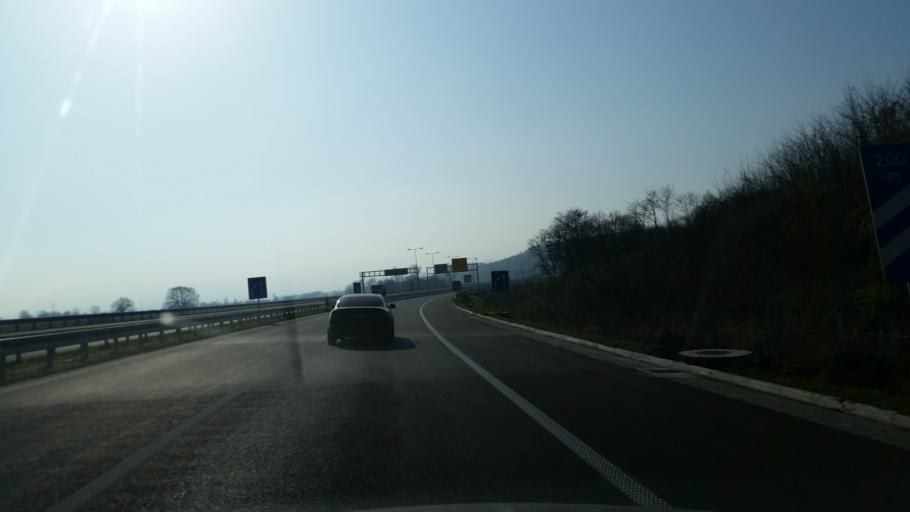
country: RS
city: Prislonica
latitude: 43.9267
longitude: 20.4012
